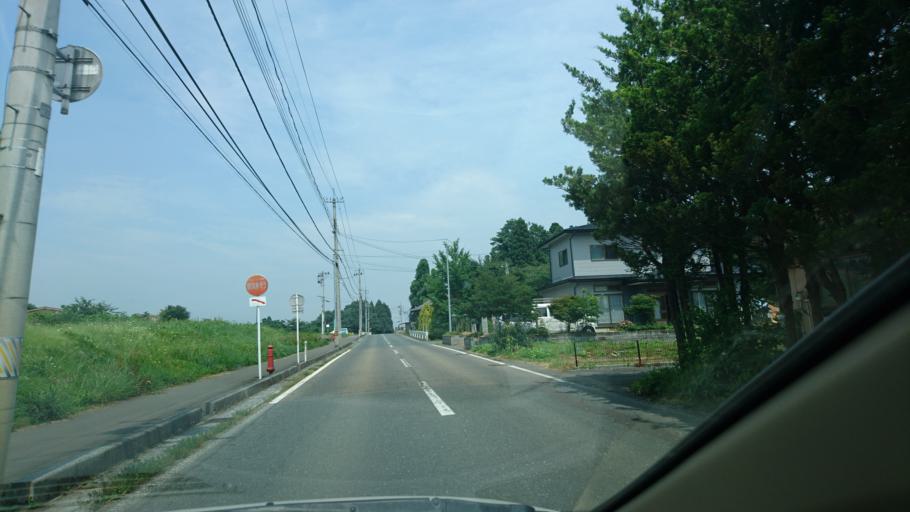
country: JP
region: Iwate
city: Kitakami
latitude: 39.2662
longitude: 141.0904
